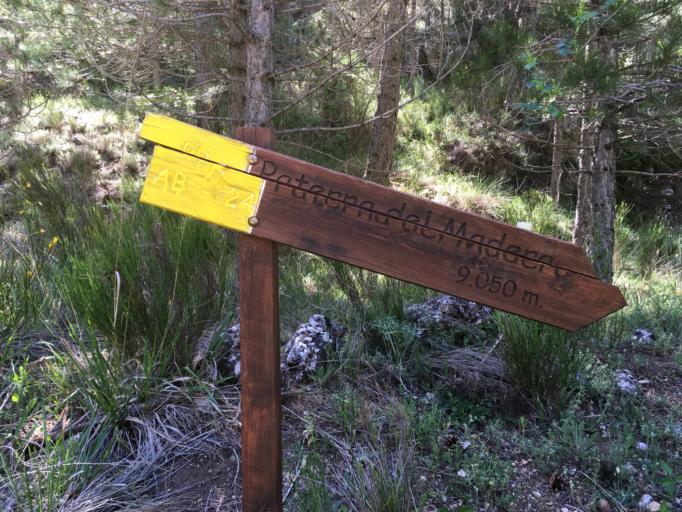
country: ES
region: Castille-La Mancha
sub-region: Provincia de Albacete
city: Paterna del Madera
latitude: 38.5452
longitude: -2.3828
